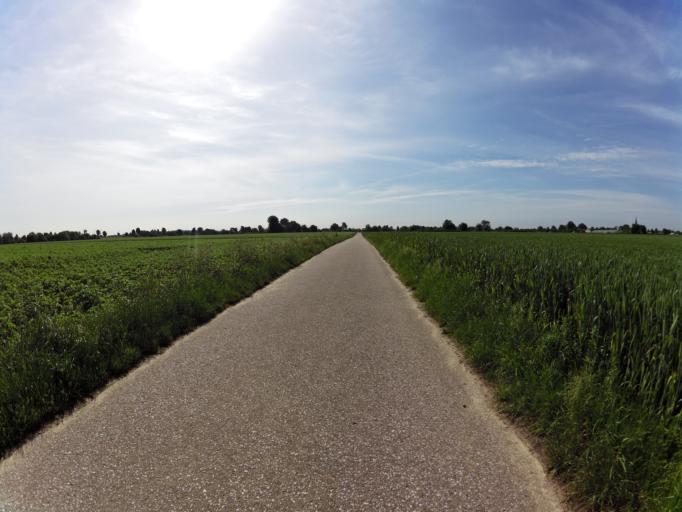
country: DE
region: North Rhine-Westphalia
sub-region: Regierungsbezirk Koln
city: Ubach-Palenberg
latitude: 50.9371
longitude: 6.0707
